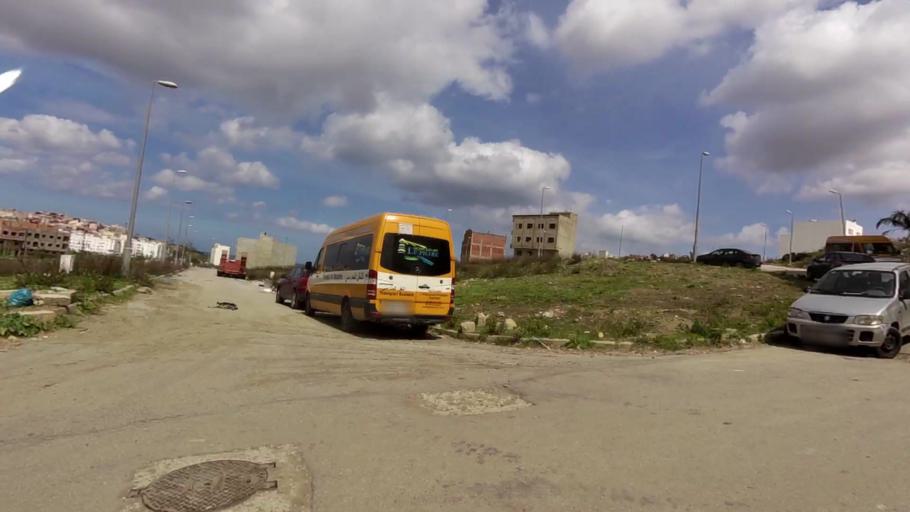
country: MA
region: Tanger-Tetouan
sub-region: Tanger-Assilah
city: Tangier
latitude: 35.7636
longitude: -5.7556
